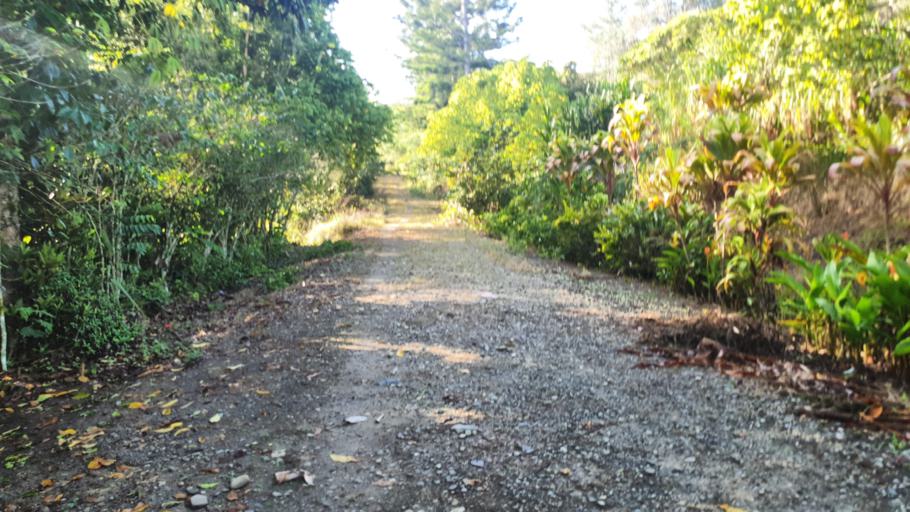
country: PG
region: Western Highlands
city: Rauna
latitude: -5.8012
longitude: 144.3670
